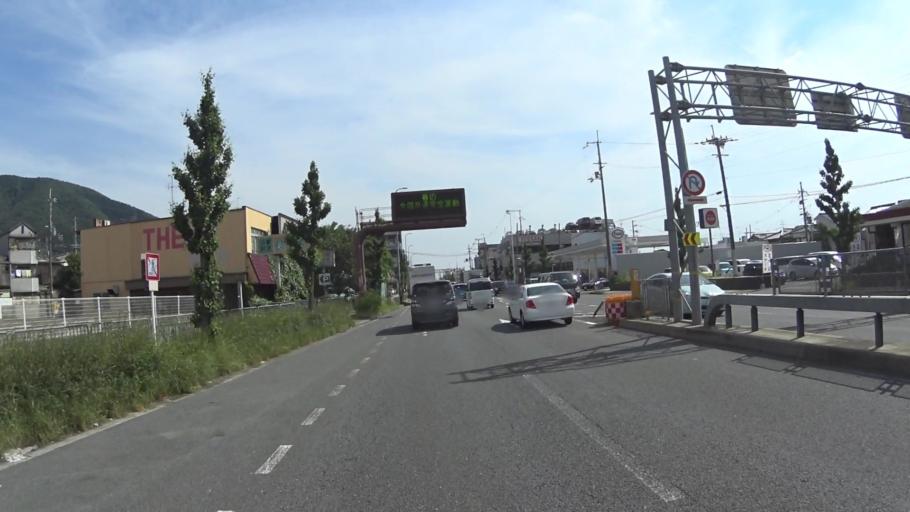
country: JP
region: Shiga Prefecture
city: Otsu-shi
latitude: 34.9873
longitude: 135.8281
